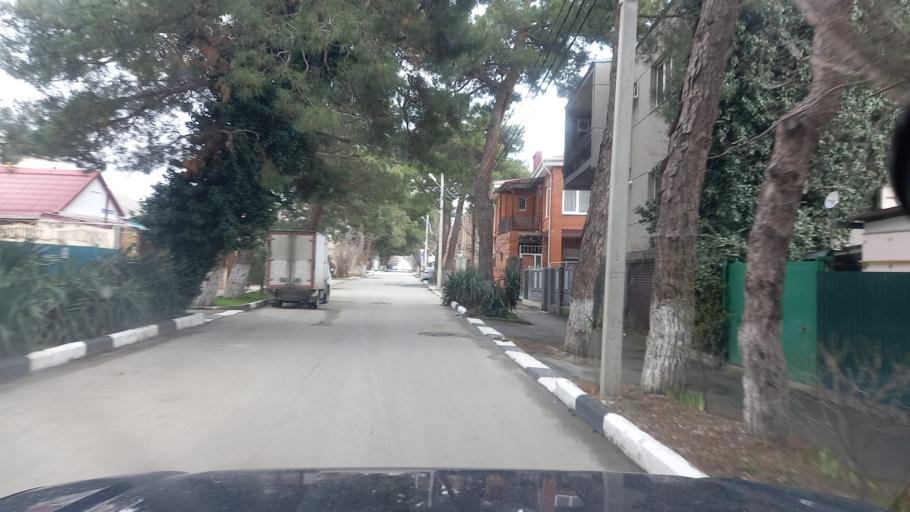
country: RU
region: Krasnodarskiy
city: Gelendzhik
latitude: 44.5600
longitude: 38.0861
